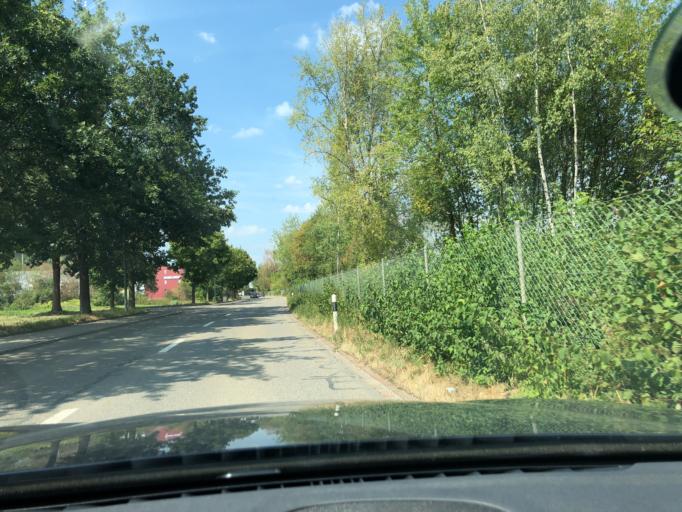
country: CH
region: Aargau
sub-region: Bezirk Bremgarten
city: Bremgarten
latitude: 47.3484
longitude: 8.3319
